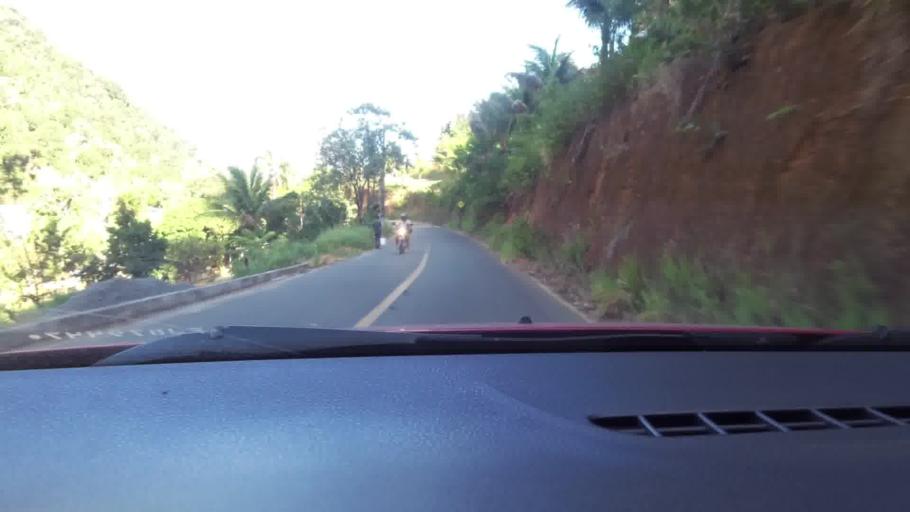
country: BR
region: Espirito Santo
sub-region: Guarapari
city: Guarapari
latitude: -20.5559
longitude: -40.5550
